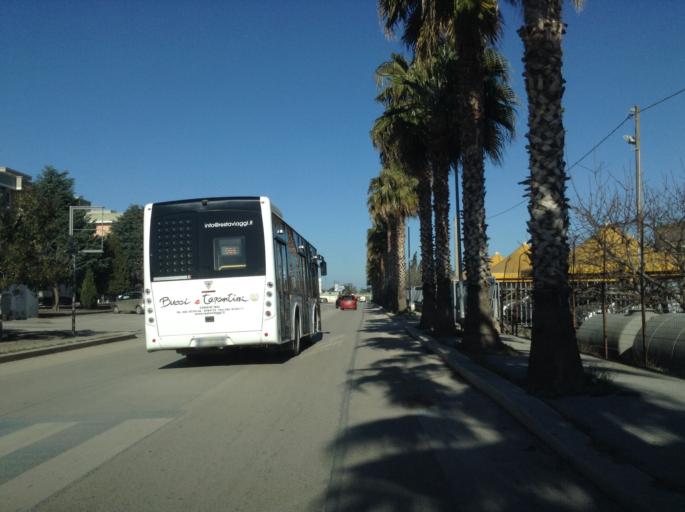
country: IT
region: Apulia
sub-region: Provincia di Bari
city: Corato
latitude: 41.1582
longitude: 16.4028
